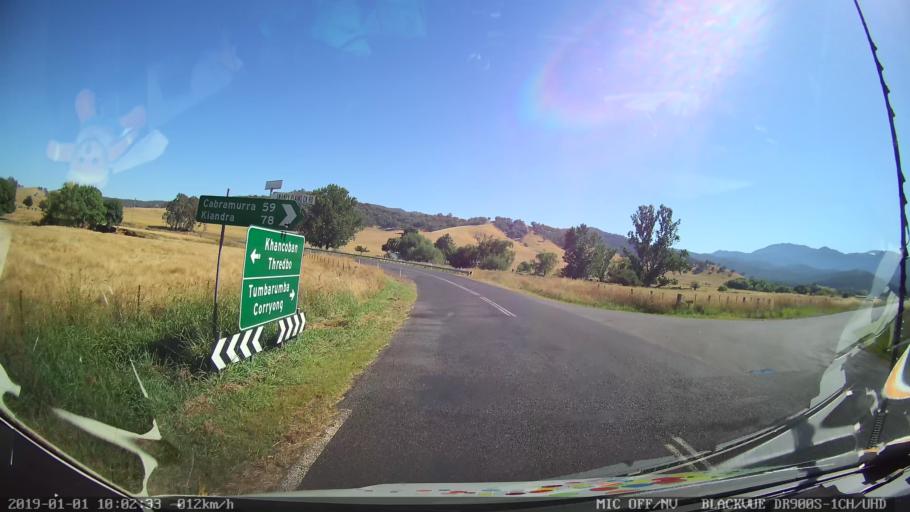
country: AU
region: New South Wales
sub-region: Snowy River
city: Jindabyne
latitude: -36.1811
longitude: 148.1021
